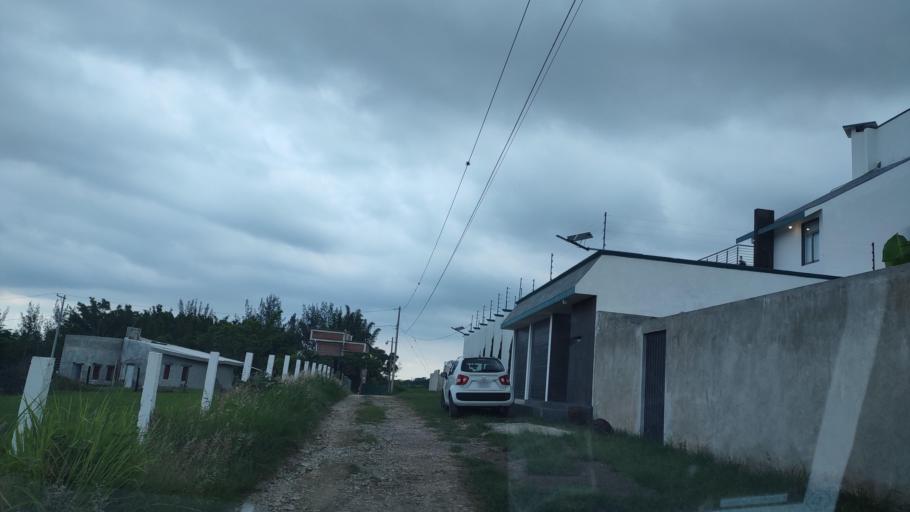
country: MX
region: Veracruz
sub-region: Emiliano Zapata
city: Dos Rios
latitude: 19.4785
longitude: -96.8198
